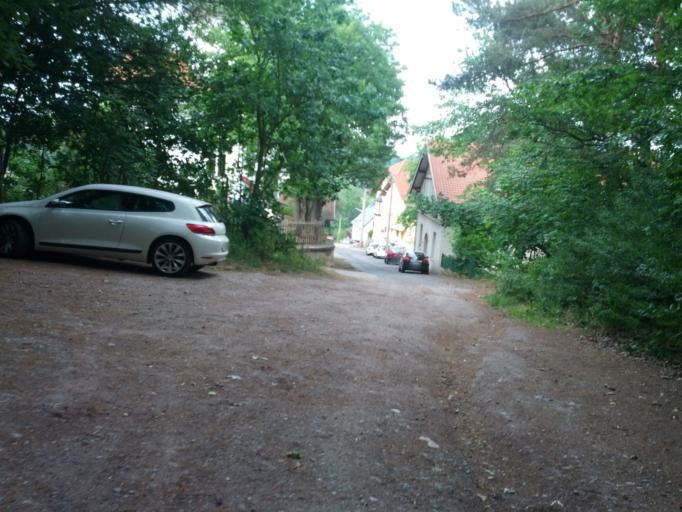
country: DE
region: Thuringia
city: Eisenach
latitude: 50.9611
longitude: 10.3199
